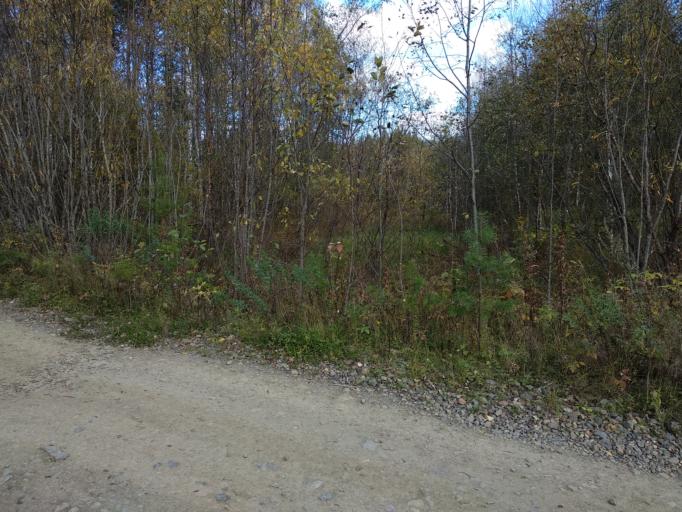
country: RU
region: Sverdlovsk
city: Rudnichnyy
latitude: 59.9647
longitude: 60.4502
